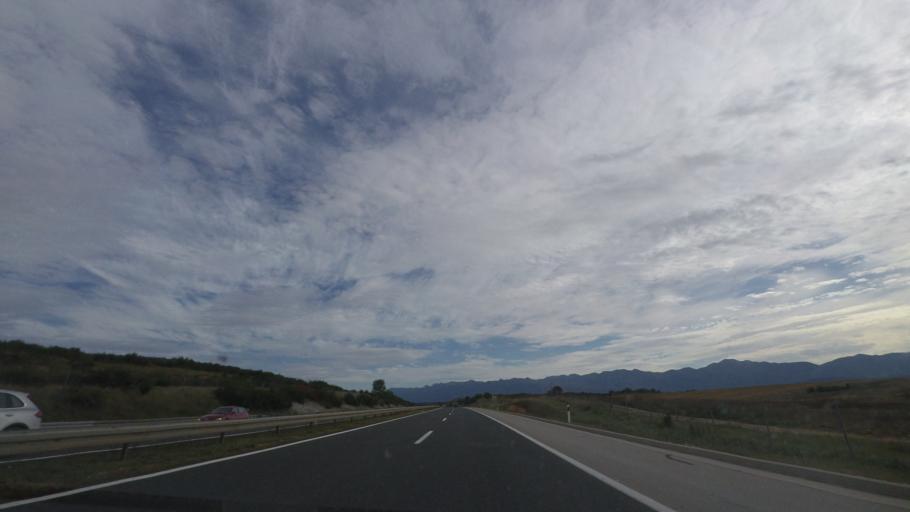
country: HR
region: Licko-Senjska
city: Gospic
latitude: 44.5616
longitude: 15.4276
